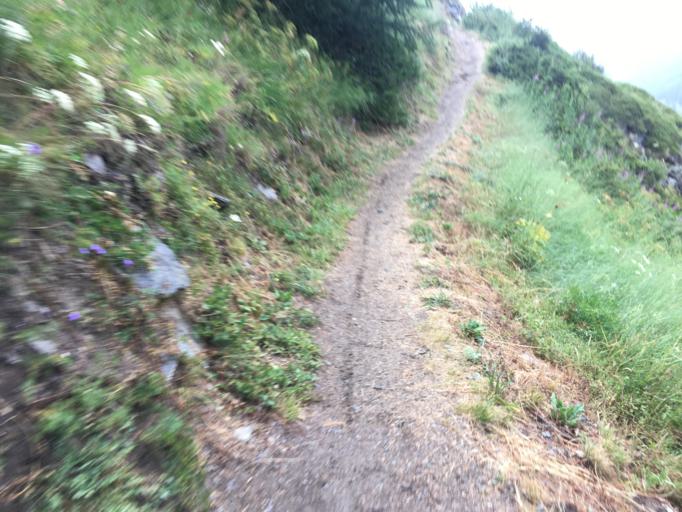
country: CH
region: Valais
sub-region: Visp District
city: Zermatt
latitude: 46.0139
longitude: 7.7370
